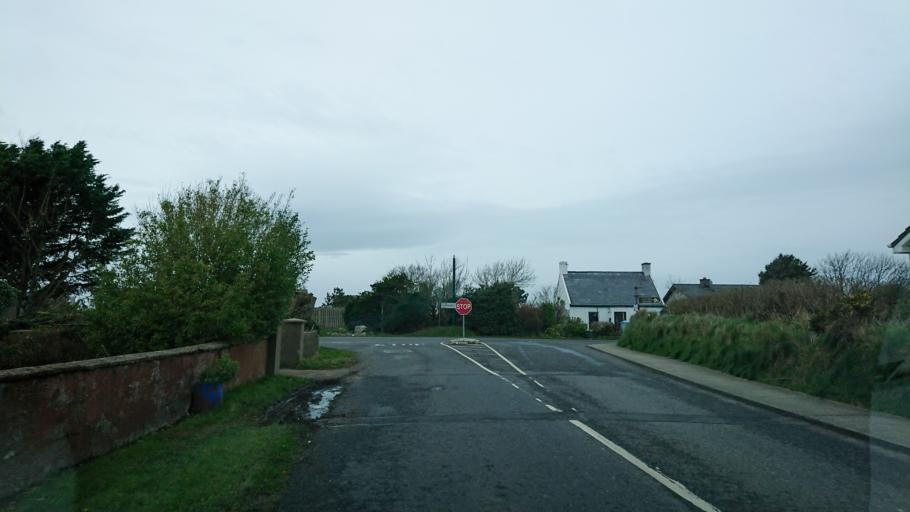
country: IE
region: Munster
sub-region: Waterford
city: Dunmore East
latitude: 52.1485
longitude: -7.0051
